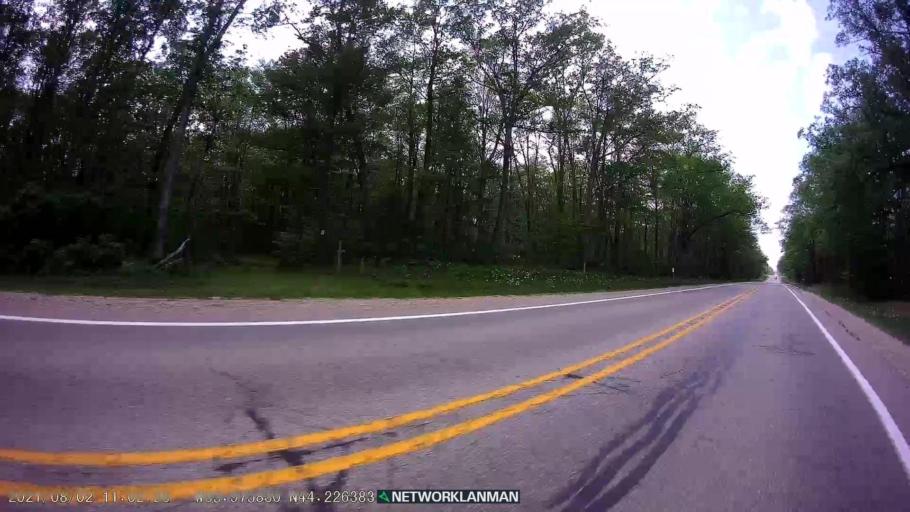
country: US
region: Michigan
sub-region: Manistee County
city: Manistee
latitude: 44.2272
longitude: -85.9769
